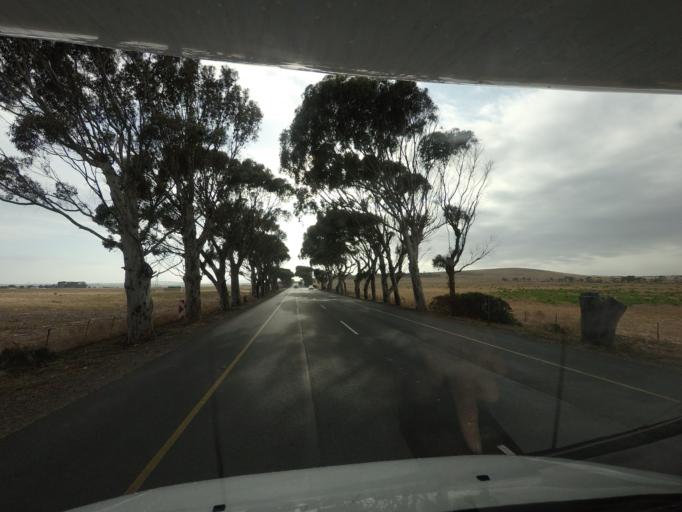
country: ZA
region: Western Cape
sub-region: City of Cape Town
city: Sunset Beach
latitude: -33.7253
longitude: 18.4688
